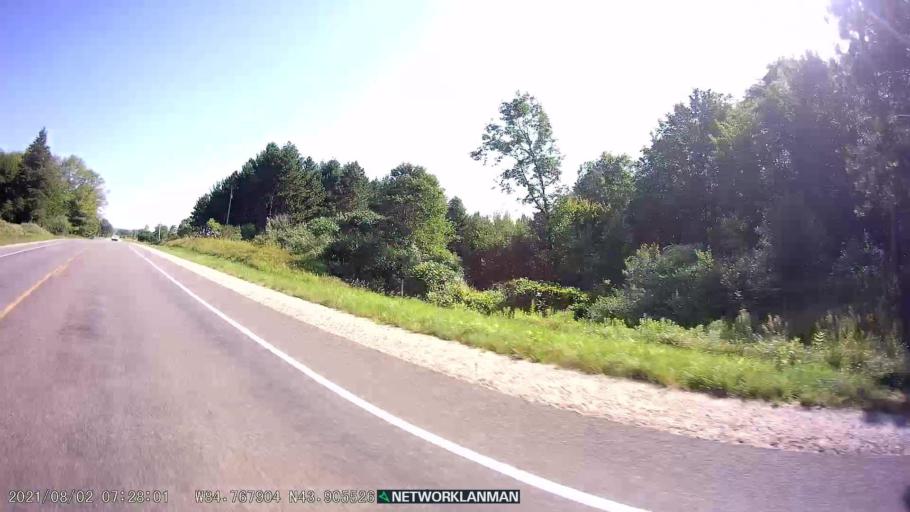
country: US
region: Michigan
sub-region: Clare County
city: Clare
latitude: 43.9056
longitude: -84.7679
